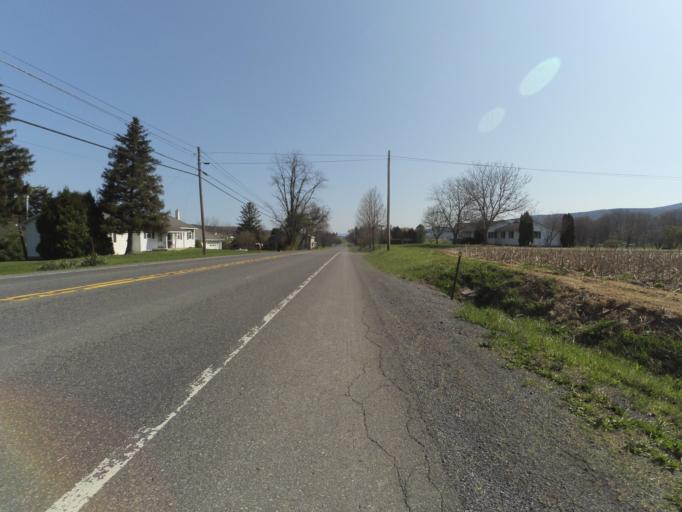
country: US
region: Pennsylvania
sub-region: Centre County
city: Zion
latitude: 40.9423
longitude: -77.6396
